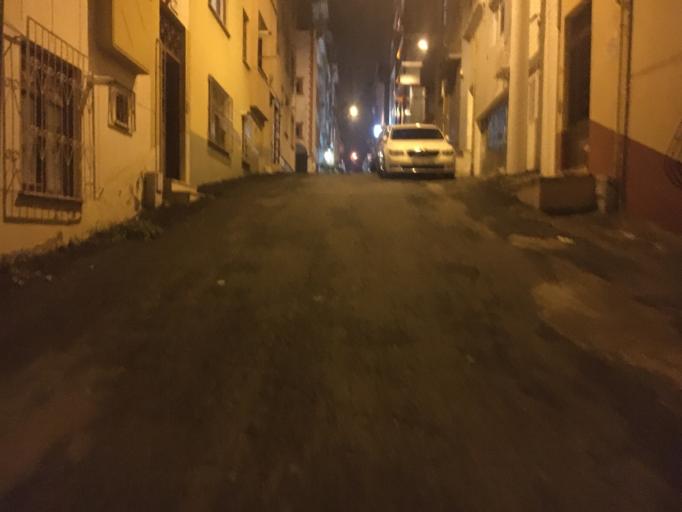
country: TR
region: Trabzon
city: Trabzon
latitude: 40.9938
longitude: 39.7786
